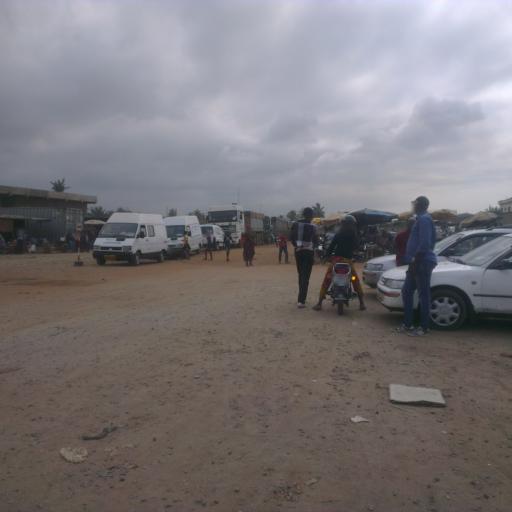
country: TG
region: Maritime
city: Lome
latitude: 6.1592
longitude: 1.2869
